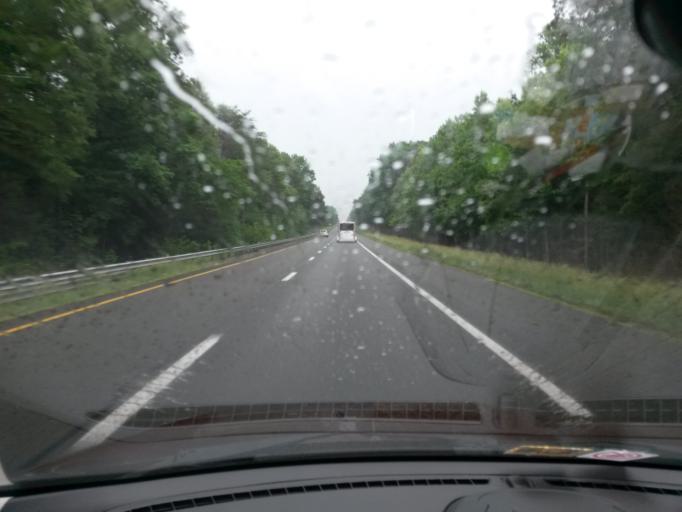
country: US
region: Virginia
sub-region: Louisa County
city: Louisa
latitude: 37.8523
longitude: -77.9914
